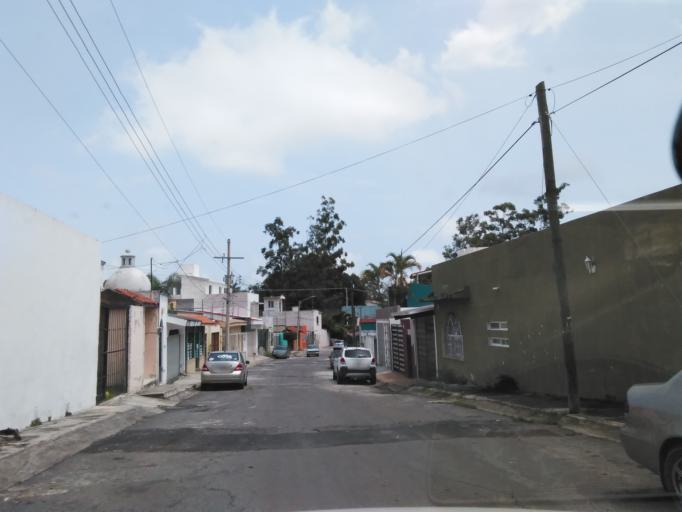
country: MX
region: Nayarit
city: Tepic
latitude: 21.5127
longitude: -104.9214
